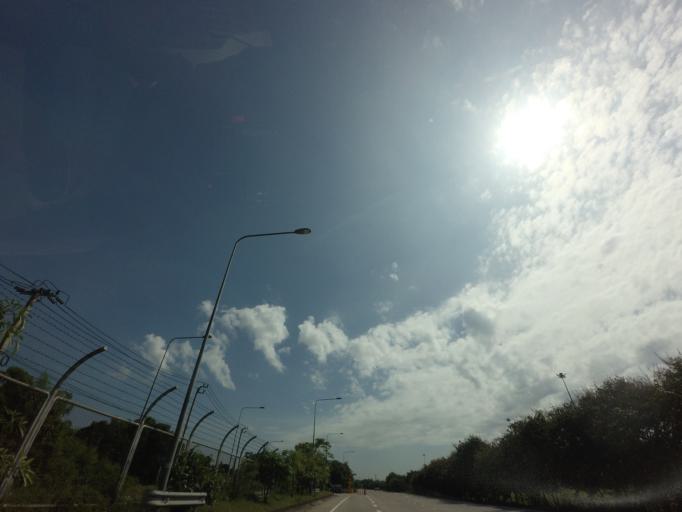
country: TH
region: Bangkok
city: Sai Mai
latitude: 13.8974
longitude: 100.6822
